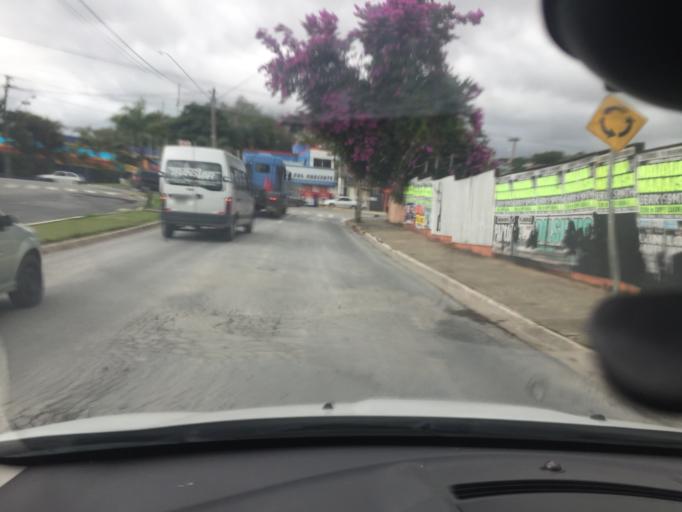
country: BR
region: Sao Paulo
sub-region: Varzea Paulista
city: Varzea Paulista
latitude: -23.2120
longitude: -46.8330
